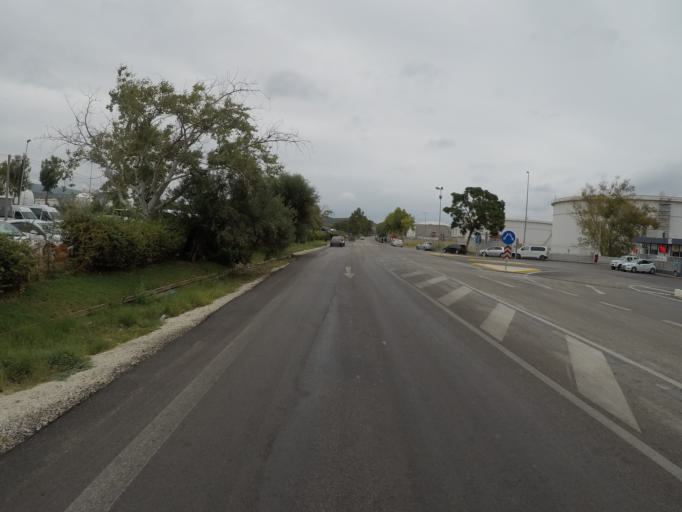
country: GR
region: Peloponnese
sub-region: Nomos Korinthias
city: Agioi Theodoroi
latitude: 37.9197
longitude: 23.0763
